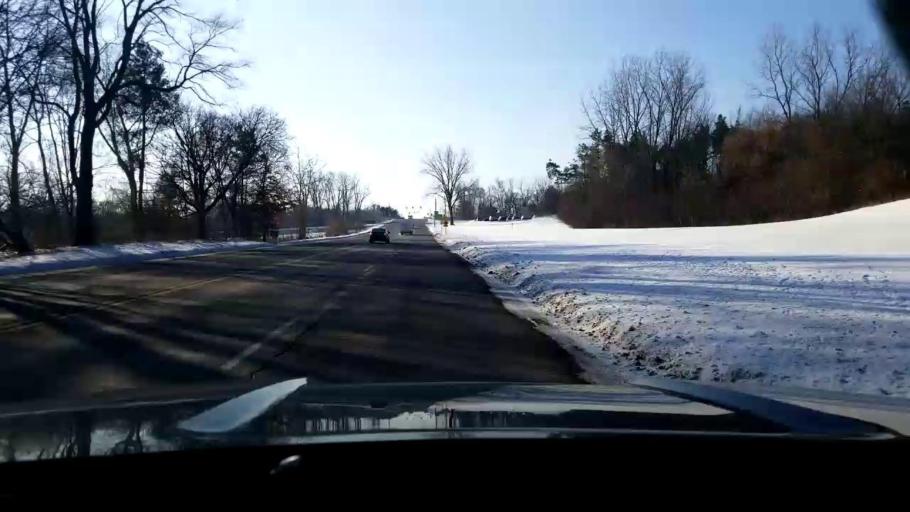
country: US
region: Michigan
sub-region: Jackson County
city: Jackson
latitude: 42.2792
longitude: -84.3844
